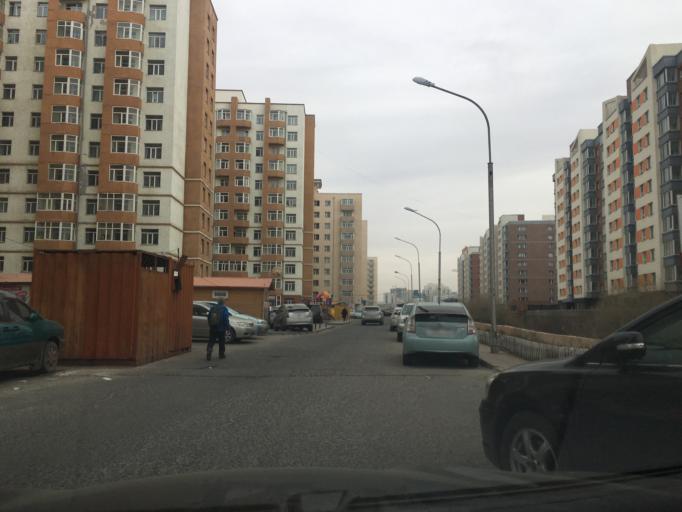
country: MN
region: Ulaanbaatar
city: Ulaanbaatar
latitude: 47.9032
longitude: 106.8855
